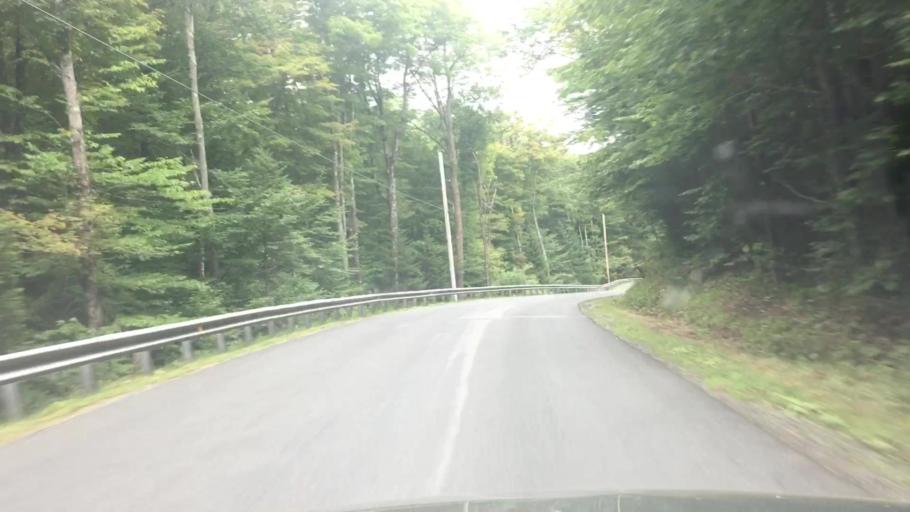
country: US
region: Vermont
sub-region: Windham County
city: Dover
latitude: 42.8429
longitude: -72.8295
